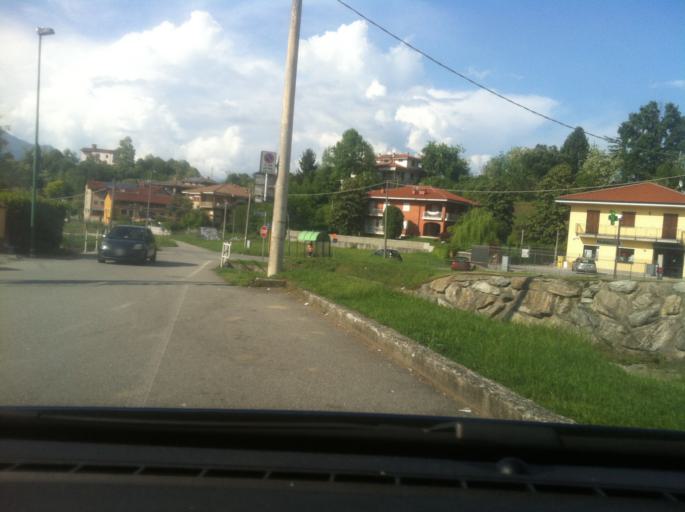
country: IT
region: Piedmont
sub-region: Provincia di Torino
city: Romano Canavese
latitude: 45.4130
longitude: 7.8500
